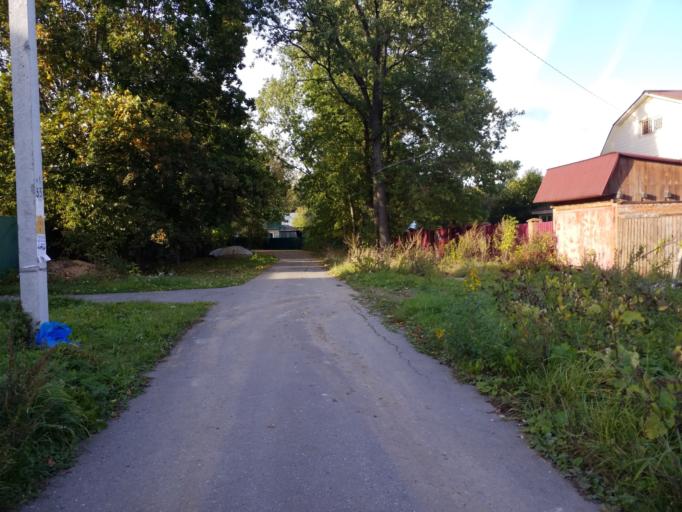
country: RU
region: Moskovskaya
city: Ashukino
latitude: 56.1664
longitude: 37.9569
